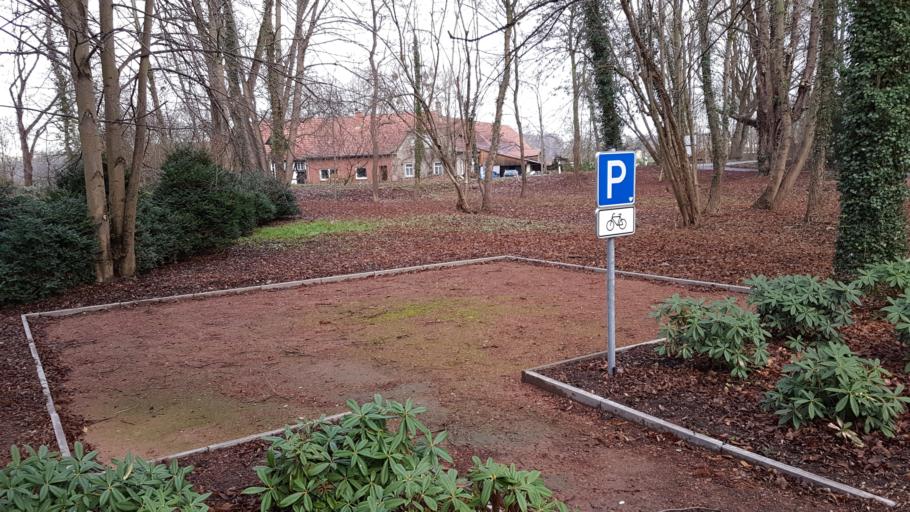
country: DE
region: North Rhine-Westphalia
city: Espelkamp
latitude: 52.3530
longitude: 8.5602
